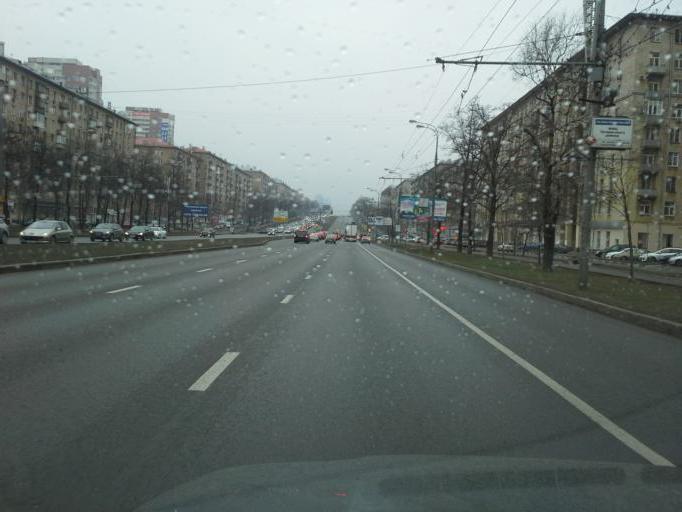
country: RU
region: Moskovskaya
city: Semenovskoye
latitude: 55.6860
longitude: 37.5421
